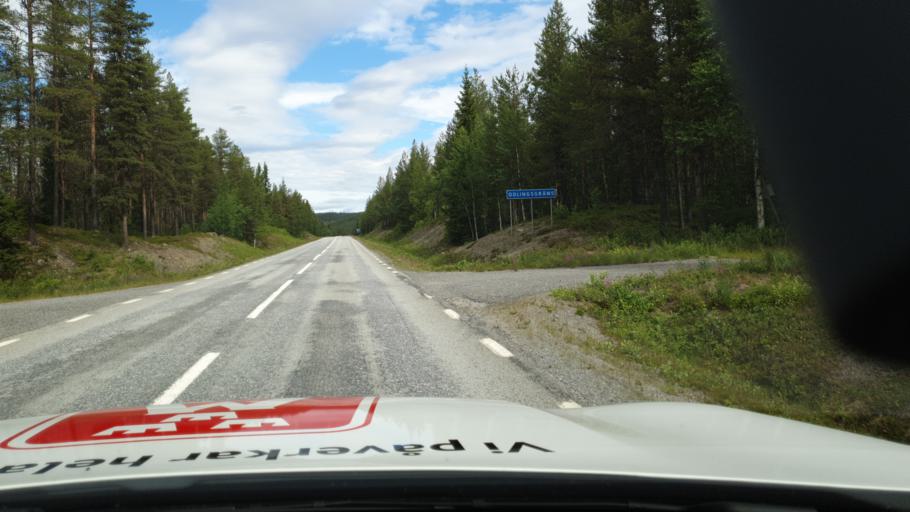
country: SE
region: Vaesterbotten
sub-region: Storumans Kommun
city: Fristad
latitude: 65.3698
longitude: 16.5187
